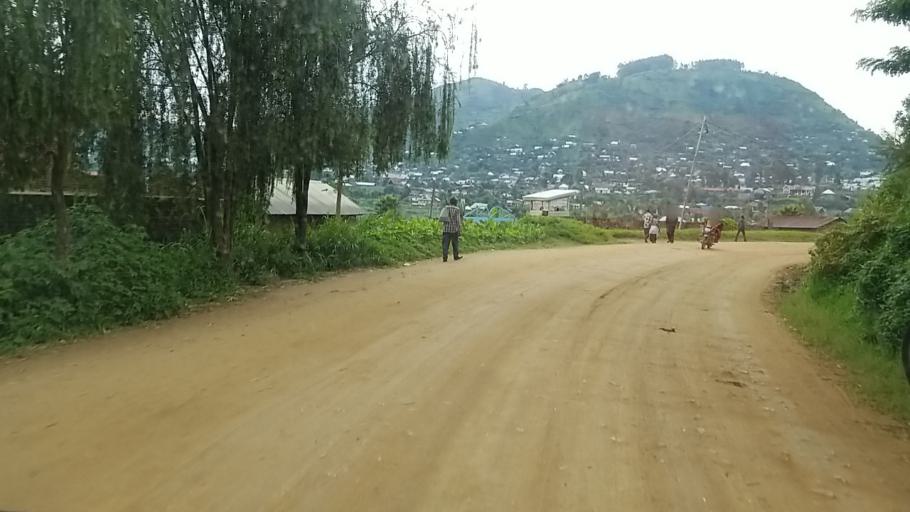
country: CD
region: Nord Kivu
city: Sake
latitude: -1.7038
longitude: 29.0181
